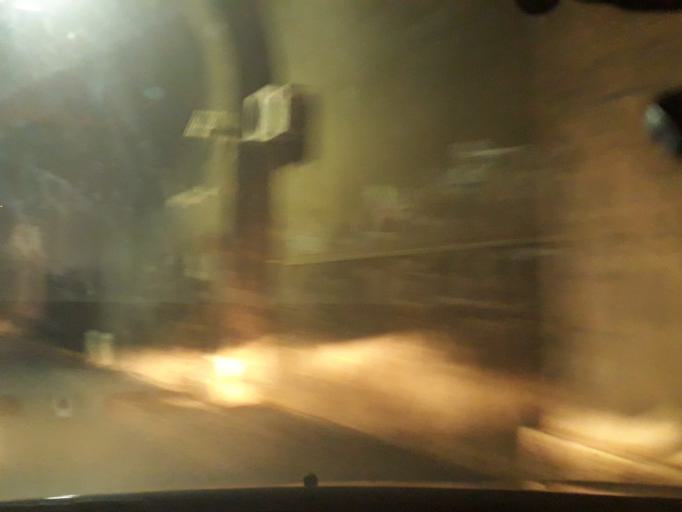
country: BA
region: Federation of Bosnia and Herzegovina
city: Kobilja Glava
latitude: 43.8560
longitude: 18.4299
